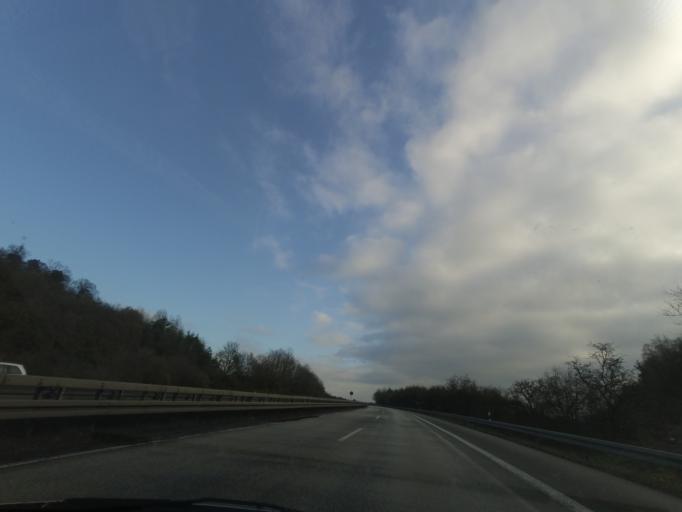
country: DE
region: Hesse
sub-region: Regierungsbezirk Giessen
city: Asslar
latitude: 50.5970
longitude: 8.4824
